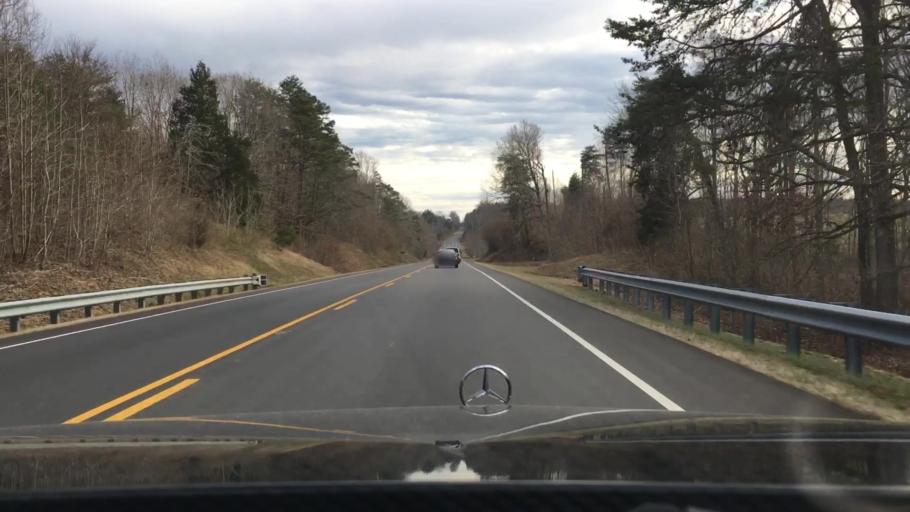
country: US
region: North Carolina
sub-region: Caswell County
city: Yanceyville
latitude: 36.4463
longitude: -79.3656
